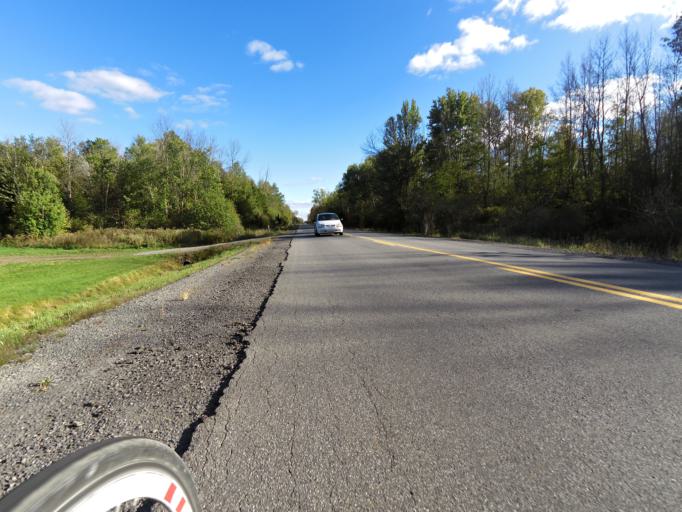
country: CA
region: Ontario
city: Bells Corners
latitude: 45.1566
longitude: -75.7804
